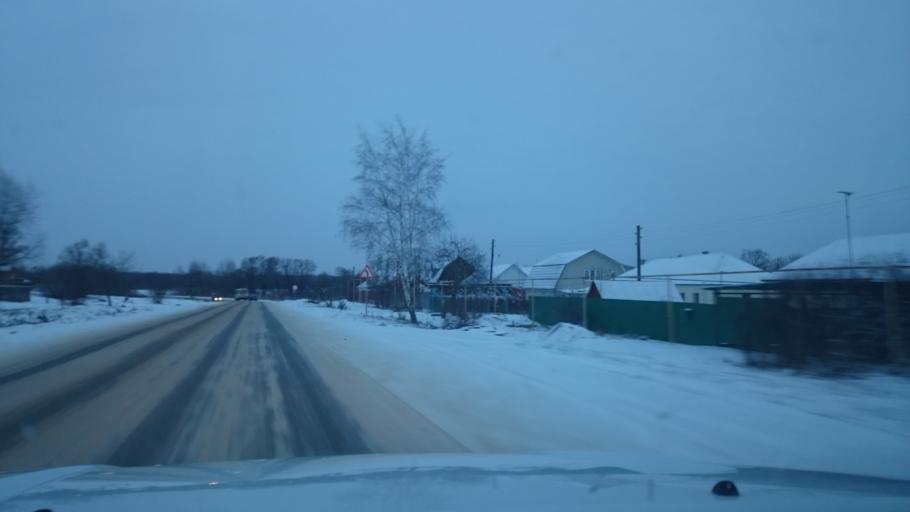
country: RU
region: Tula
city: Leninskiy
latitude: 54.2524
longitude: 37.3709
